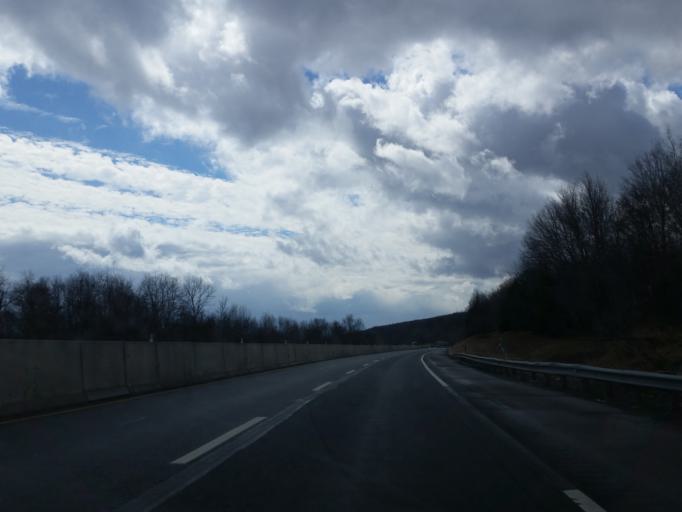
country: US
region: Pennsylvania
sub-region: Lackawanna County
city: Taylor
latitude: 41.4288
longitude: -75.7065
